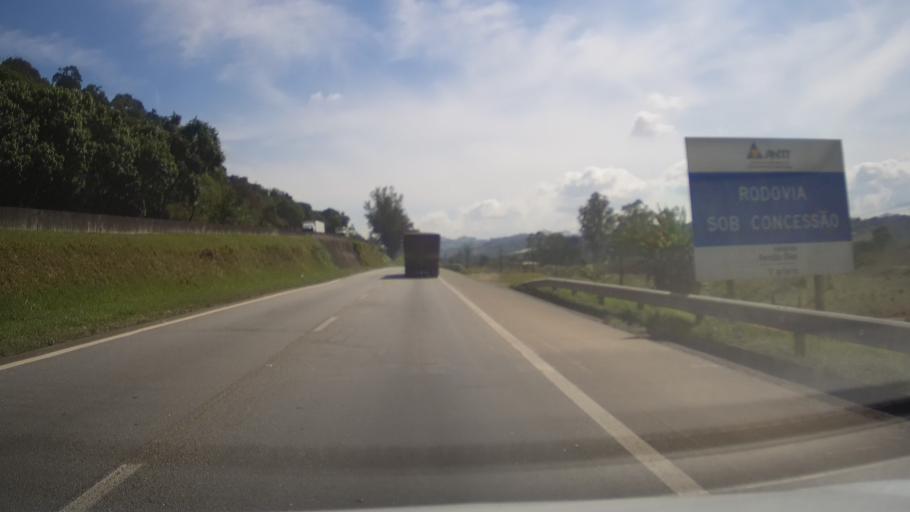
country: BR
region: Minas Gerais
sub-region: Cambui
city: Cambui
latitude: -22.5889
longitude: -46.0515
